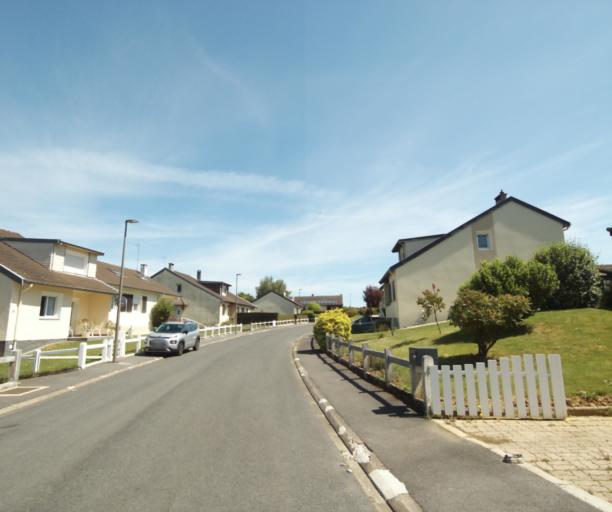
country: FR
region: Champagne-Ardenne
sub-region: Departement des Ardennes
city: La Francheville
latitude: 49.7452
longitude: 4.7100
